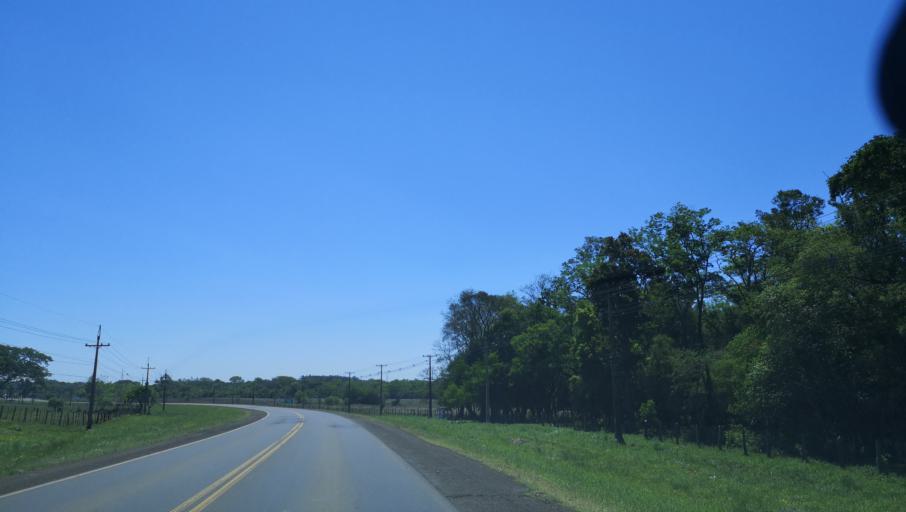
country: PY
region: Itapua
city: Carmen del Parana
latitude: -27.1965
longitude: -56.1848
